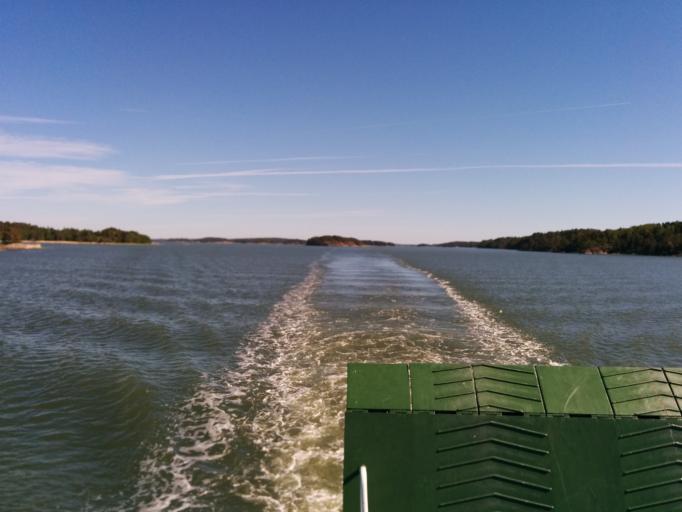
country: FI
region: Varsinais-Suomi
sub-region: Turku
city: Velkua
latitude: 60.4539
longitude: 21.7032
